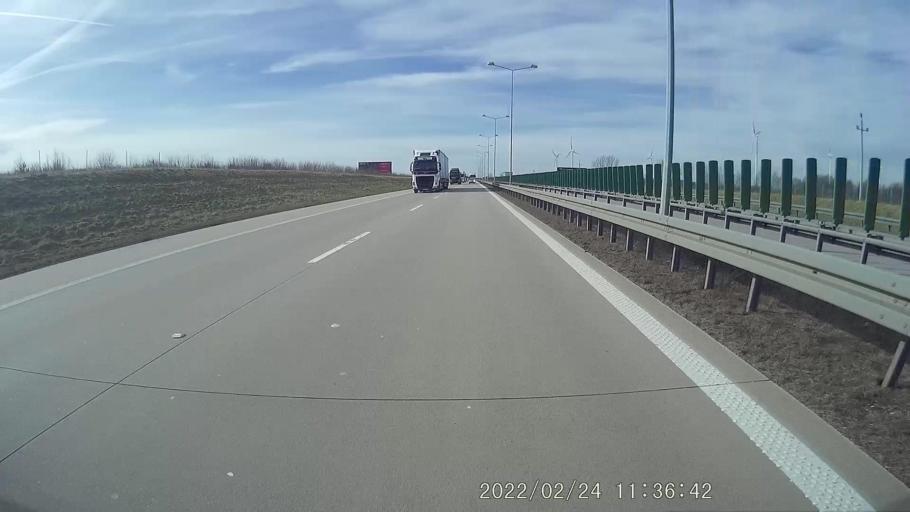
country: PL
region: Lower Silesian Voivodeship
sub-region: Powiat polkowicki
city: Przemkow
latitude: 51.5216
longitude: 15.8116
